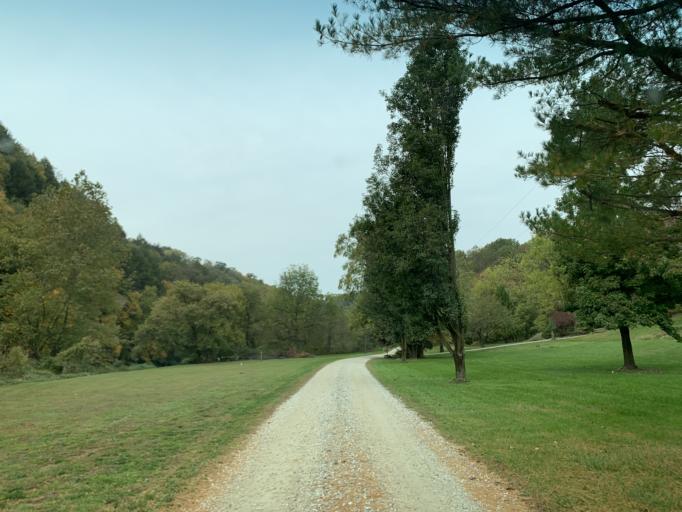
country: US
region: Pennsylvania
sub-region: York County
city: Susquehanna Trails
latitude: 39.7936
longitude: -76.4246
